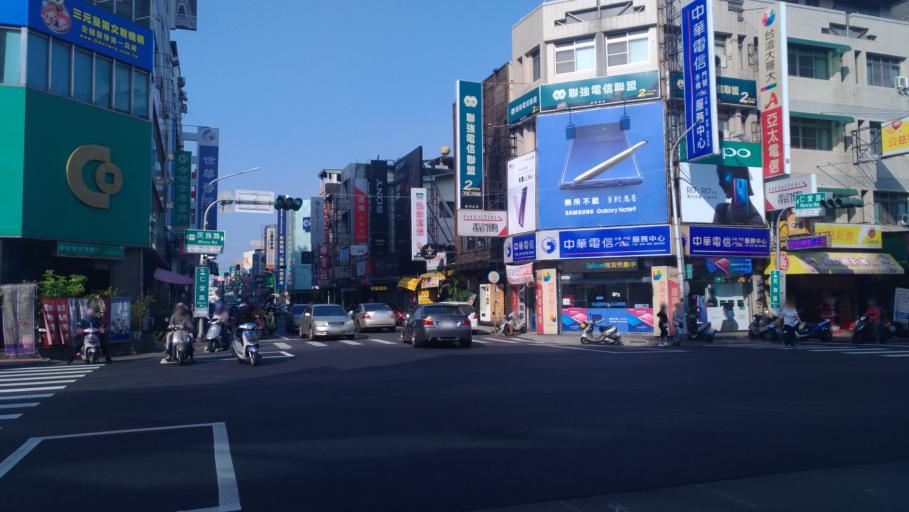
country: TW
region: Taiwan
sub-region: Chiayi
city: Jiayi Shi
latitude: 23.4753
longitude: 120.4422
